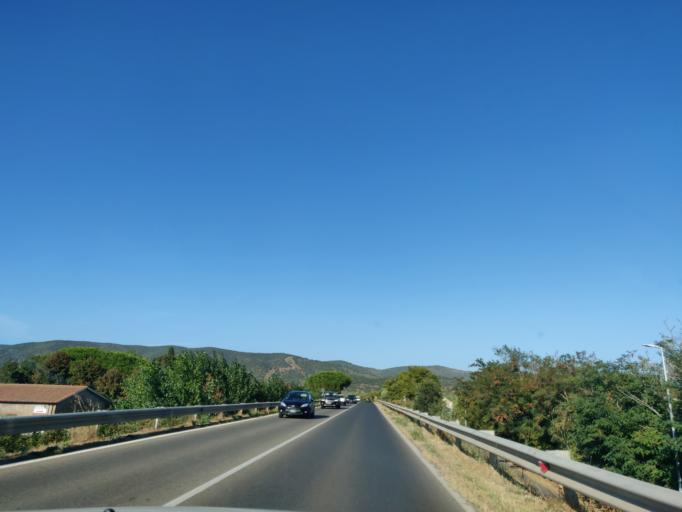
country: IT
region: Tuscany
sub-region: Provincia di Grosseto
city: Orbetello Scalo
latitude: 42.4459
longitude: 11.2405
